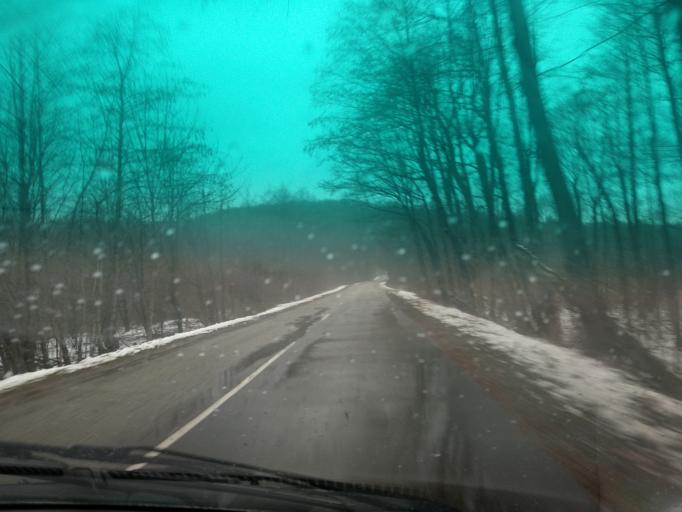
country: RU
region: Krasnodarskiy
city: Khadyzhensk
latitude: 44.2268
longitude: 39.3871
